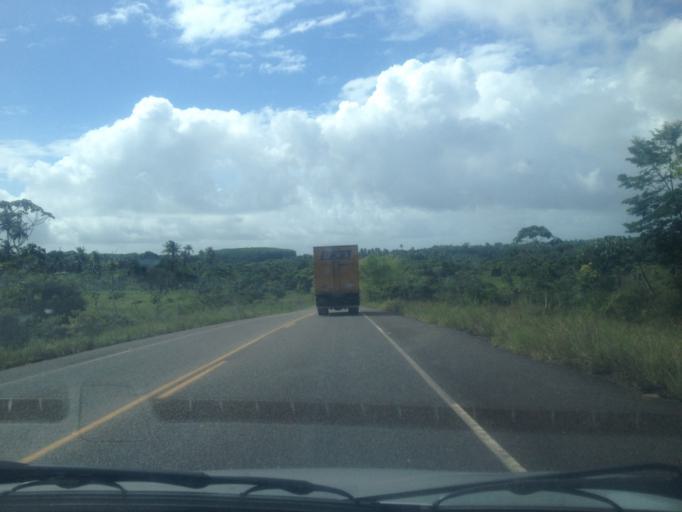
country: BR
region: Sergipe
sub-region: Indiaroba
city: Indiaroba
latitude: -11.6572
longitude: -37.5497
